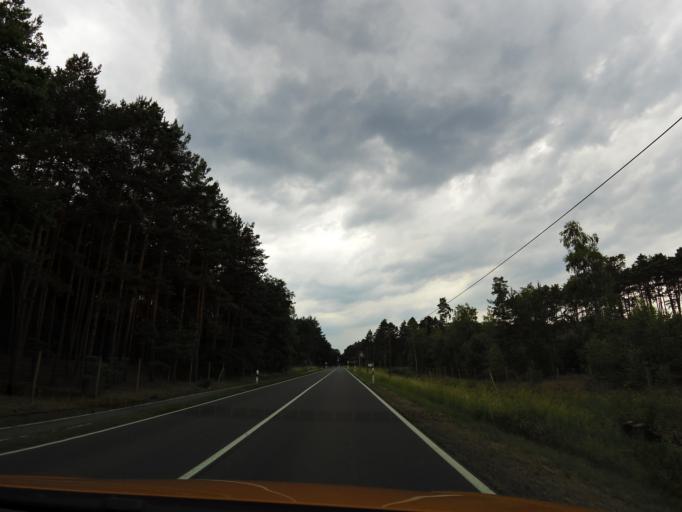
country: DE
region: Brandenburg
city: Baruth
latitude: 52.0311
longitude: 13.5297
